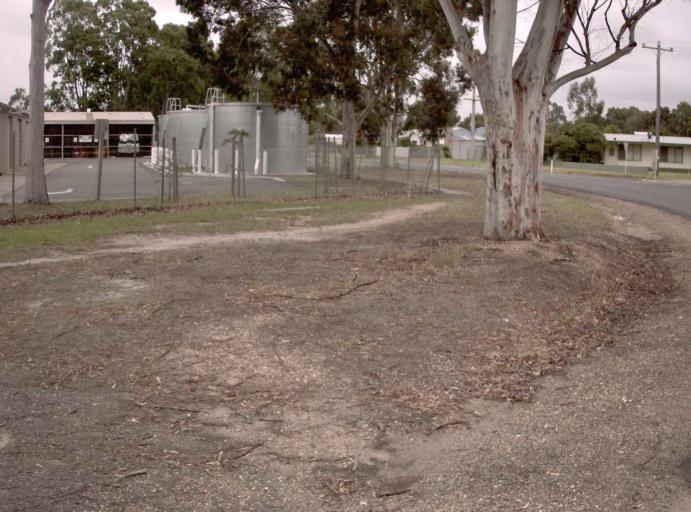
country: AU
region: Victoria
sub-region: Wellington
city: Heyfield
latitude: -37.9766
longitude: 146.7832
